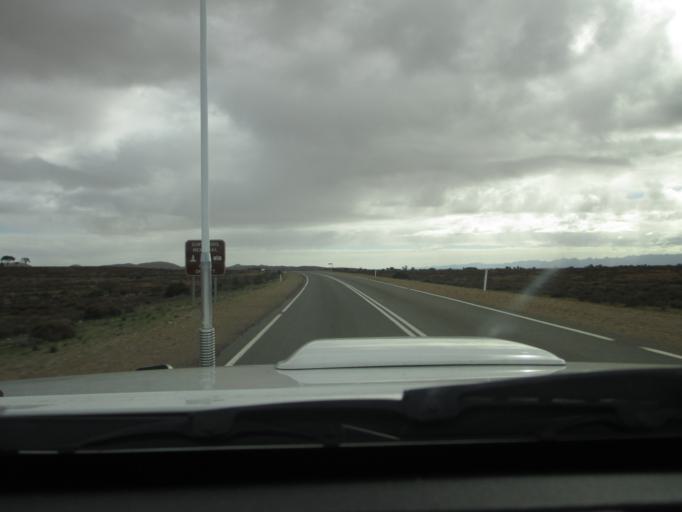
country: AU
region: South Australia
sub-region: Flinders Ranges
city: Quorn
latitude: -31.5573
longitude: 138.4285
